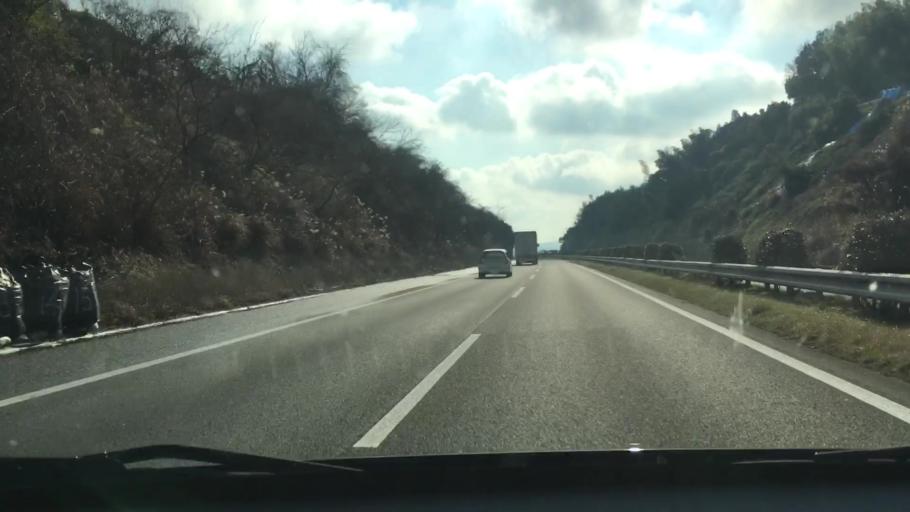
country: JP
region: Kumamoto
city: Kumamoto
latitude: 32.7273
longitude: 130.7732
